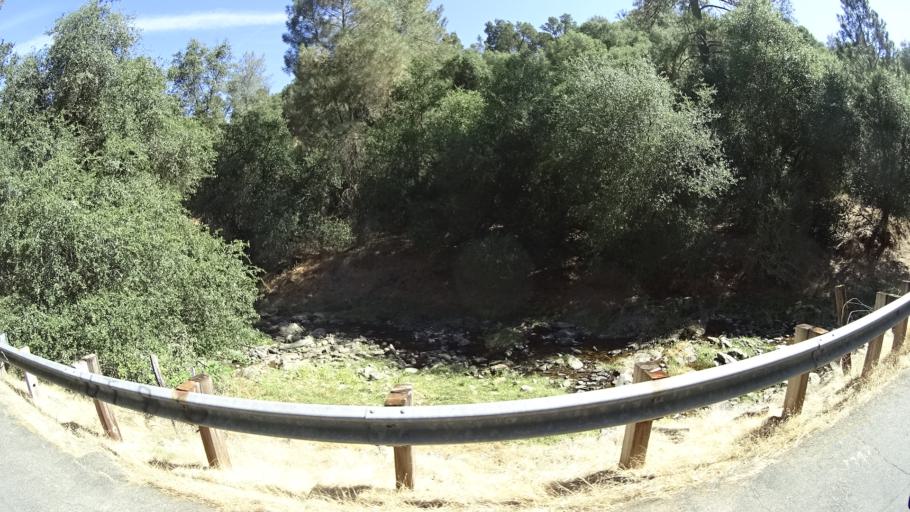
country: US
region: California
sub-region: Calaveras County
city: Angels Camp
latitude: 38.1459
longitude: -120.5694
